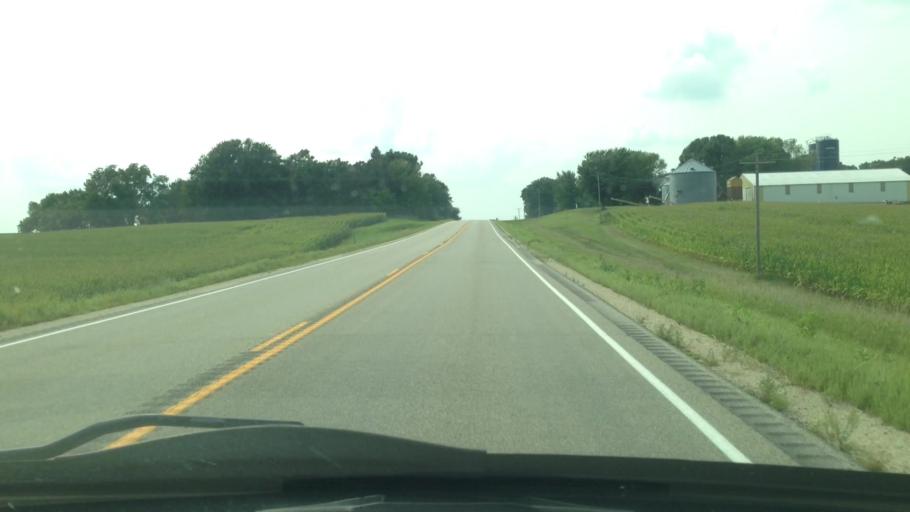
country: US
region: Minnesota
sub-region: Wabasha County
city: Plainview
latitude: 44.1653
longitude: -92.2127
